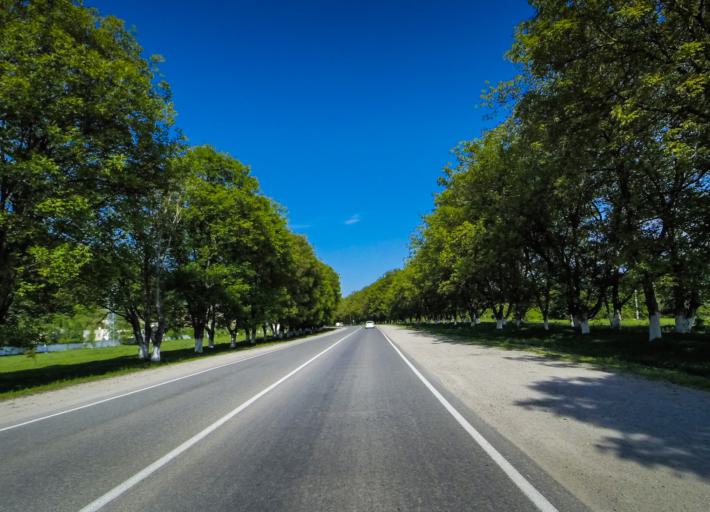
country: RU
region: Kabardino-Balkariya
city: Kashkhatau
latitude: 43.3299
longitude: 43.6379
